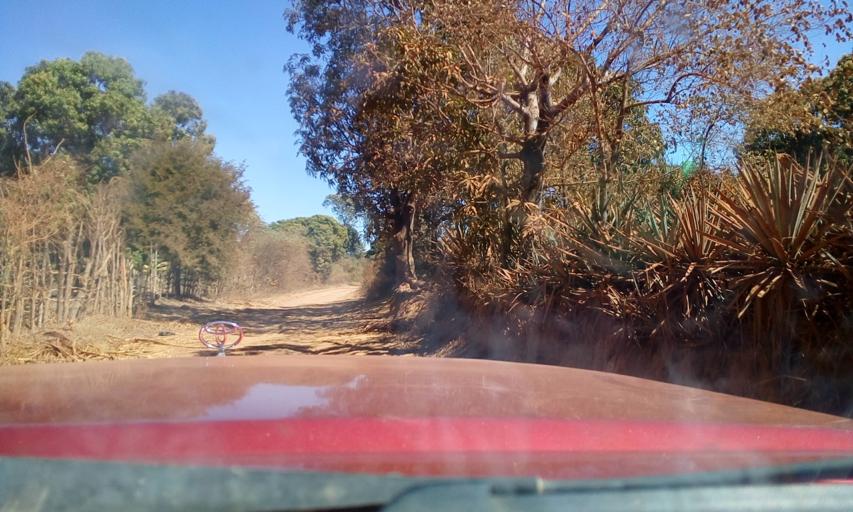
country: MG
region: Boeny
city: Mahajanga
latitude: -15.9615
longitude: 45.9616
